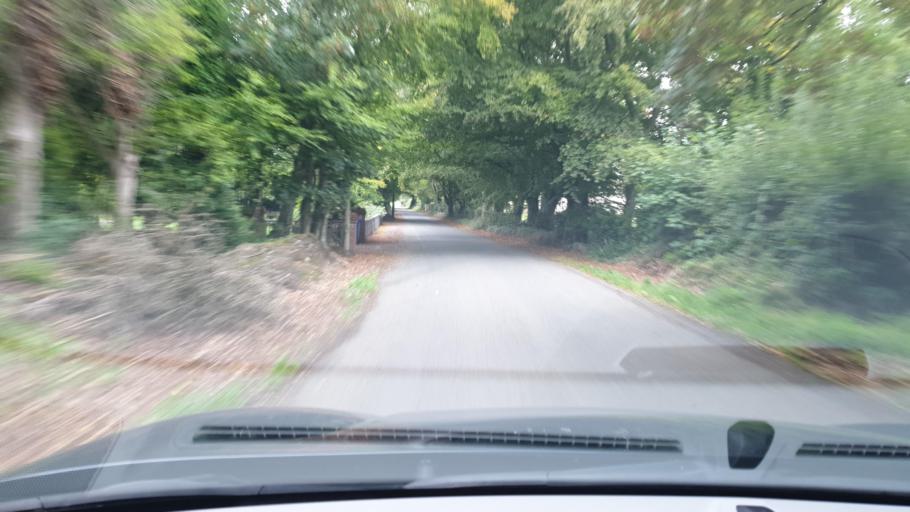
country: IE
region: Leinster
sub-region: An Mhi
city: Dunshaughlin
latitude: 53.5601
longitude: -6.5140
